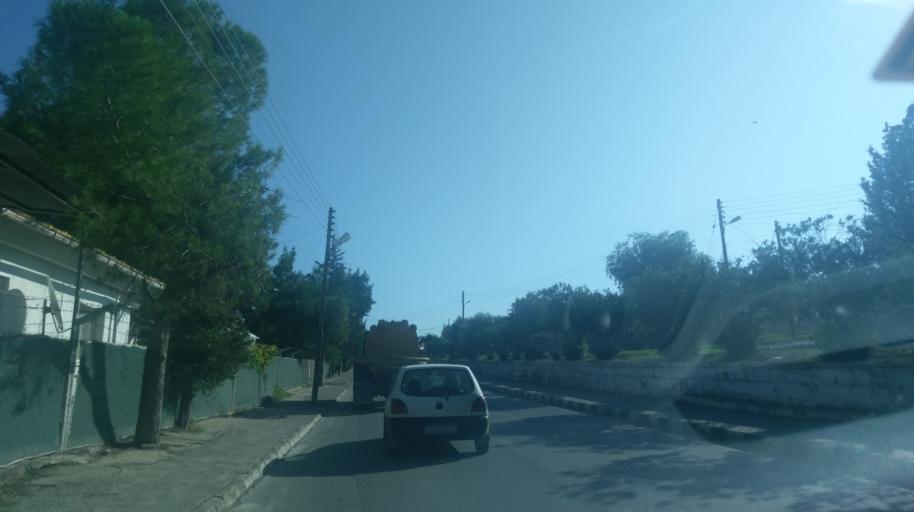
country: CY
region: Keryneia
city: Kyrenia
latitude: 35.2661
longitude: 33.3248
